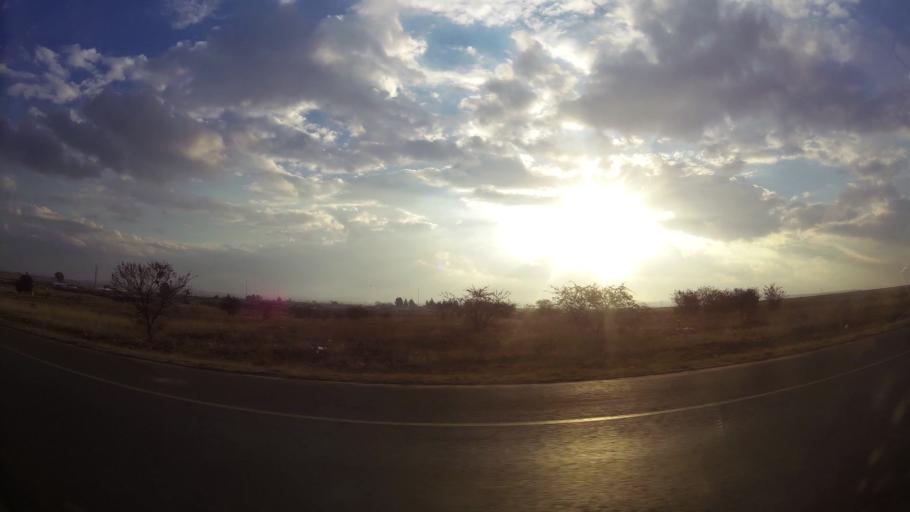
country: ZA
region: Gauteng
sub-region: Sedibeng District Municipality
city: Vanderbijlpark
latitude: -26.6003
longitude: 27.8184
